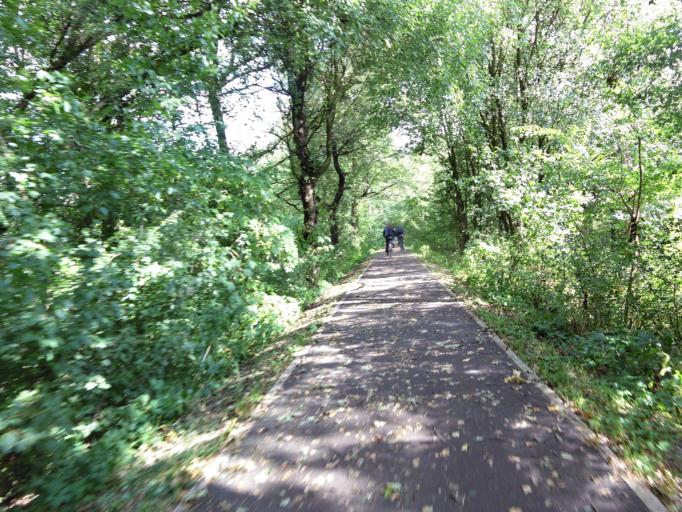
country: DE
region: Saxony-Anhalt
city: Vockerode
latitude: 51.8670
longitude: 12.3157
